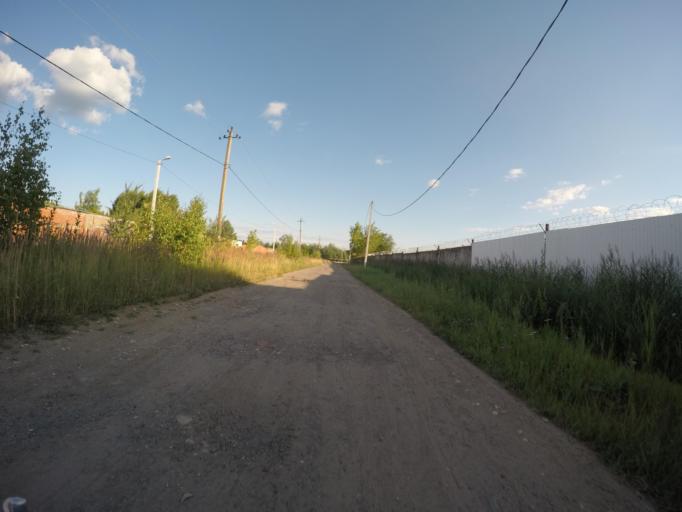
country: RU
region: Moskovskaya
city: Rechitsy
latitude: 55.5934
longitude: 38.4967
